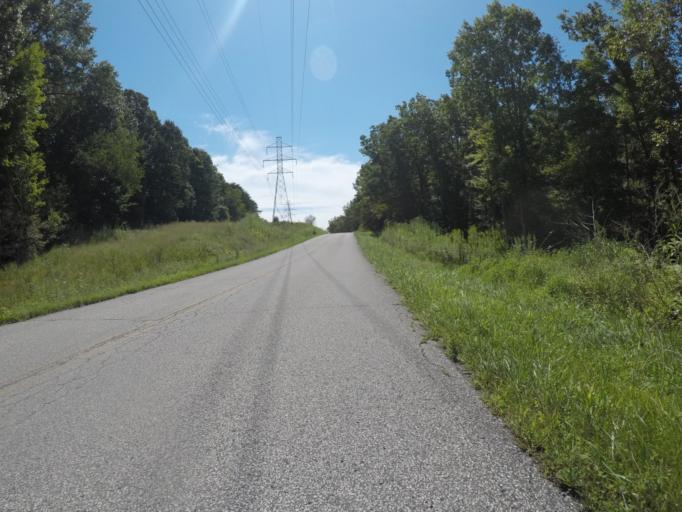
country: US
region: Kentucky
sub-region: Boyd County
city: Catlettsburg
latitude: 38.4069
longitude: -82.6529
